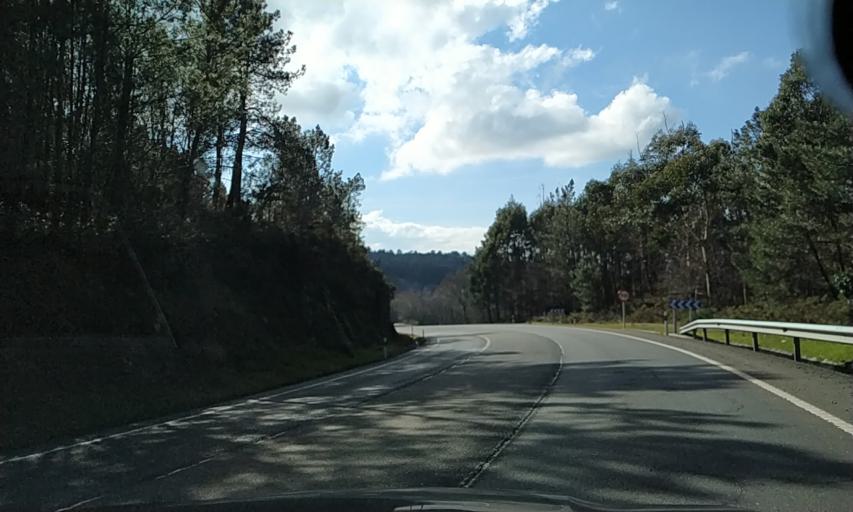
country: ES
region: Galicia
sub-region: Provincia da Coruna
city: Ribeira
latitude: 42.7150
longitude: -8.3661
